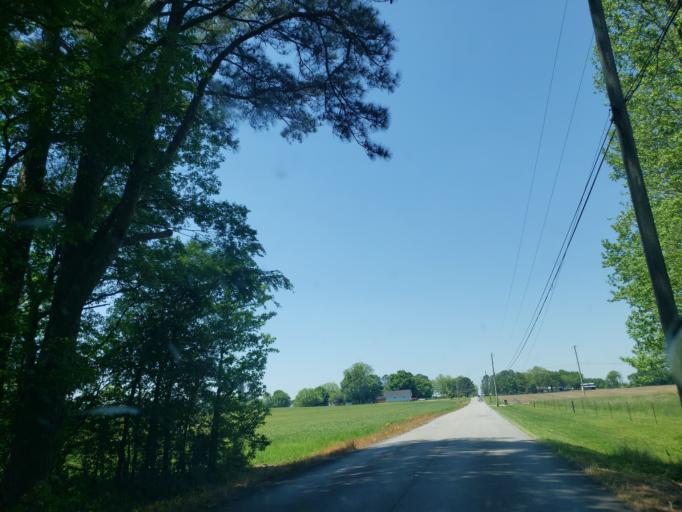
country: US
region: Alabama
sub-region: Madison County
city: Hazel Green
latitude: 34.9617
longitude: -86.5911
